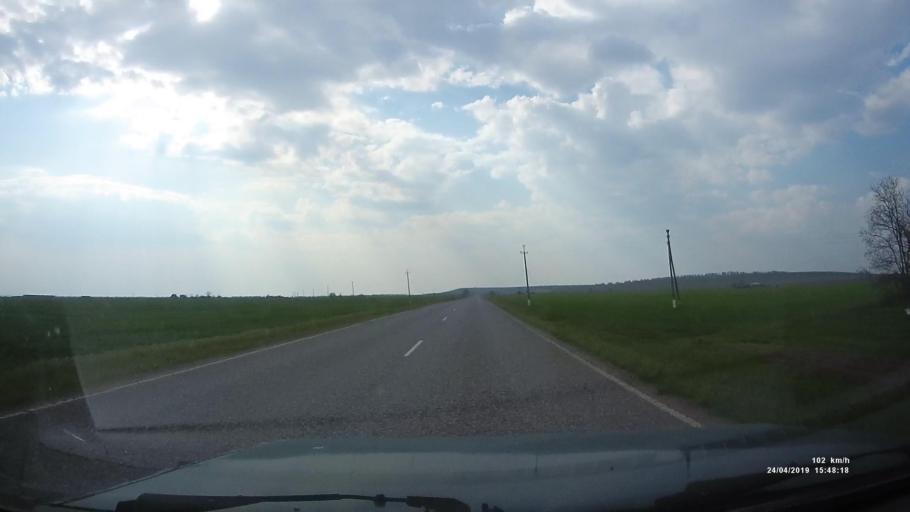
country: RU
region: Kalmykiya
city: Yashalta
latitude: 46.5980
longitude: 42.6787
